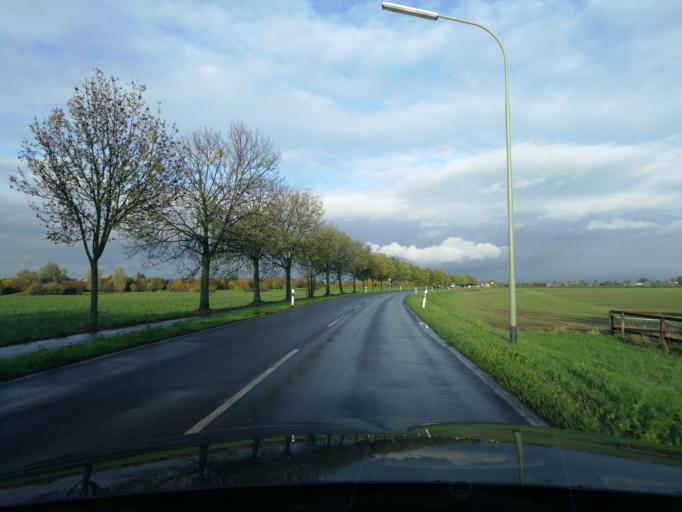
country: DE
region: North Rhine-Westphalia
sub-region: Regierungsbezirk Dusseldorf
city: Neuss
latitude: 51.1291
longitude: 6.7402
